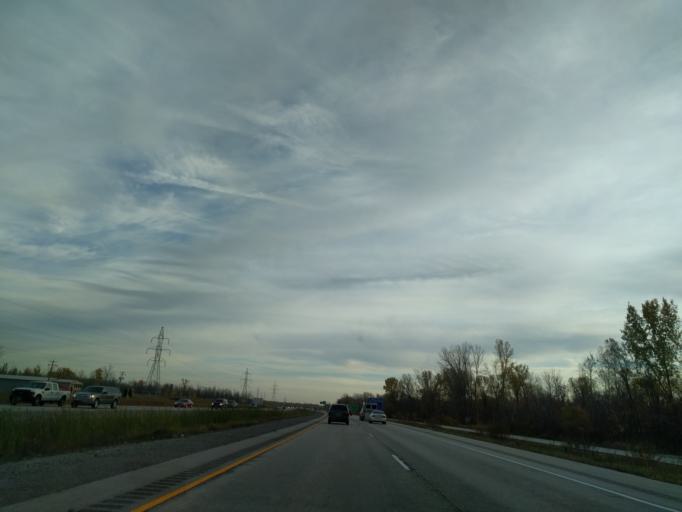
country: US
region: Wisconsin
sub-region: Brown County
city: Suamico
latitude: 44.6028
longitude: -88.0504
